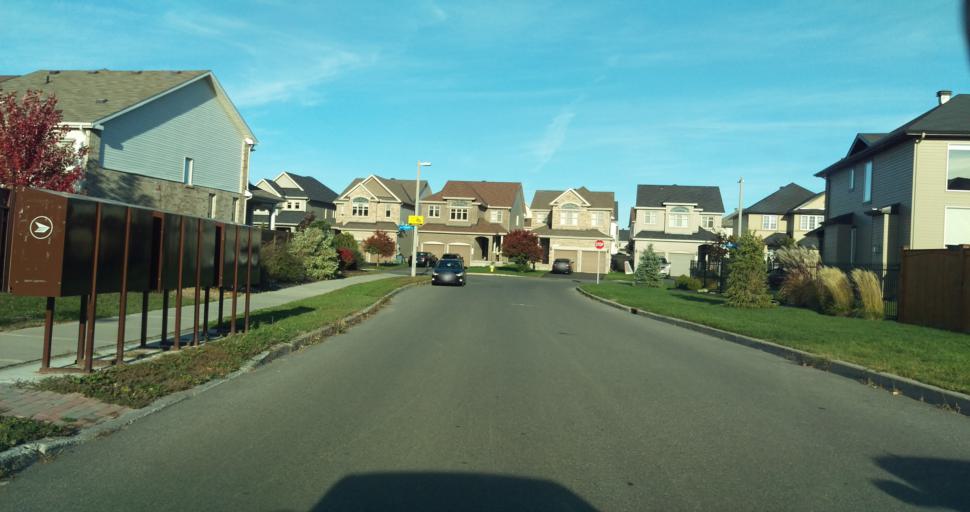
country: CA
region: Ontario
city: Clarence-Rockland
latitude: 45.4573
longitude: -75.4607
